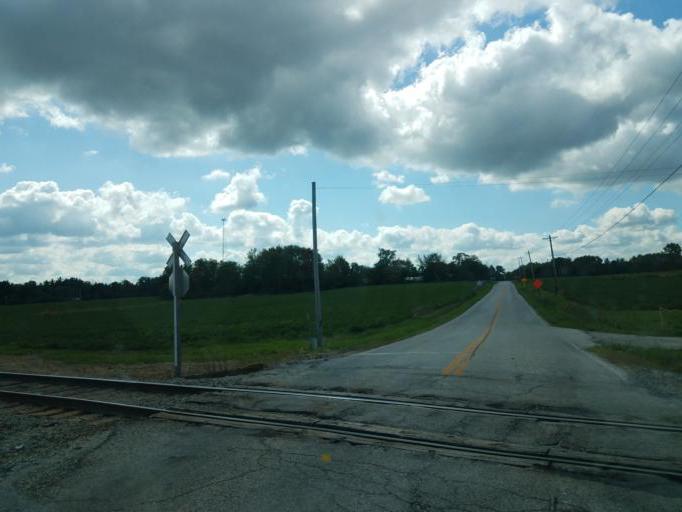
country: US
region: Ohio
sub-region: Medina County
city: Lodi
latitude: 41.1029
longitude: -82.0945
